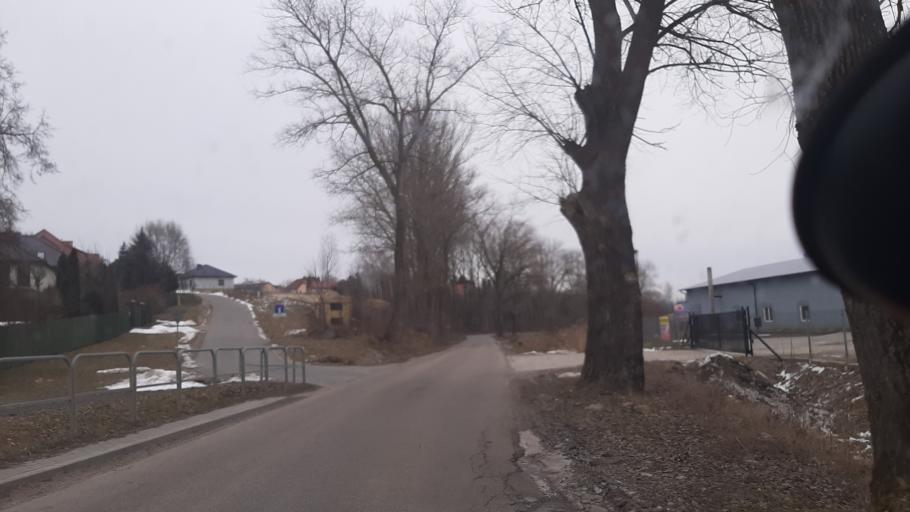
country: PL
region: Lublin Voivodeship
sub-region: Powiat lubelski
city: Jakubowice Murowane
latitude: 51.2821
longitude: 22.6053
